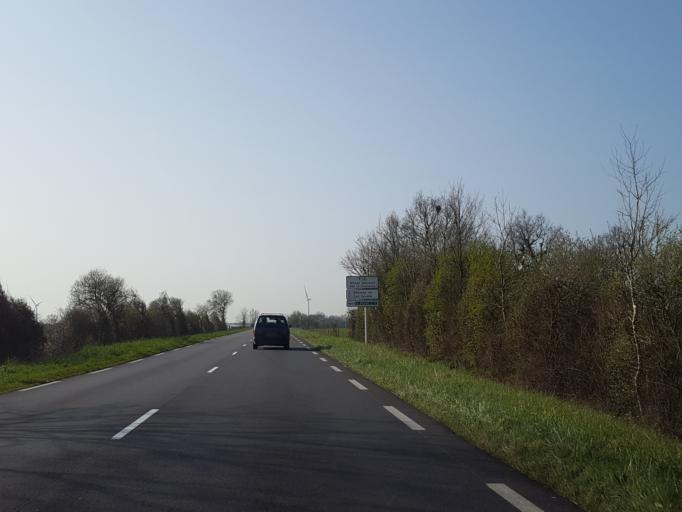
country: FR
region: Pays de la Loire
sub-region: Departement de la Loire-Atlantique
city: Geneston
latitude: 47.0260
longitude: -1.5052
